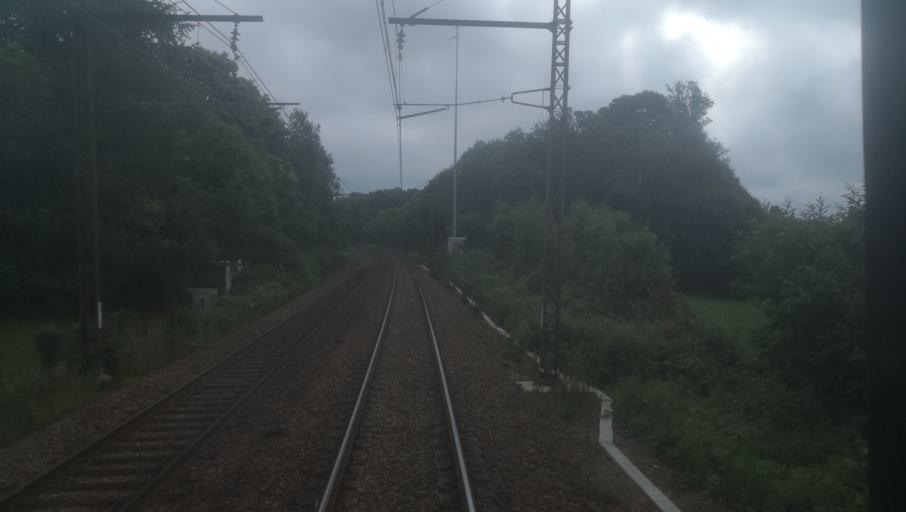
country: FR
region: Limousin
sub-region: Departement de la Haute-Vienne
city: Ambazac
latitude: 45.9653
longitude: 1.4499
